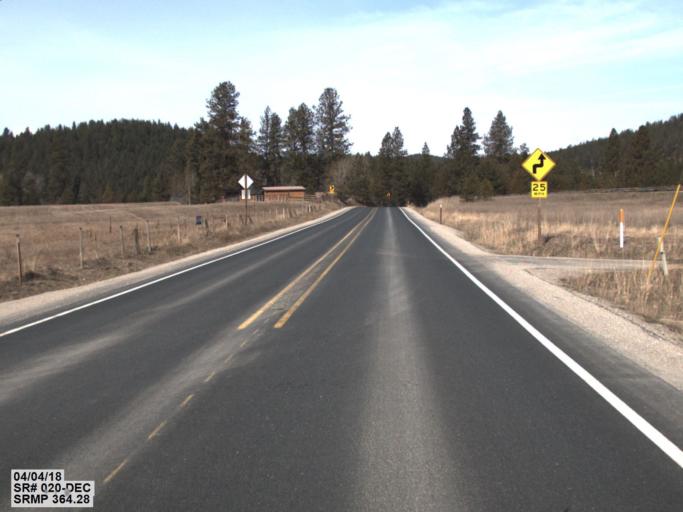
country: US
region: Washington
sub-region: Stevens County
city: Colville
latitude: 48.5100
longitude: -117.7260
